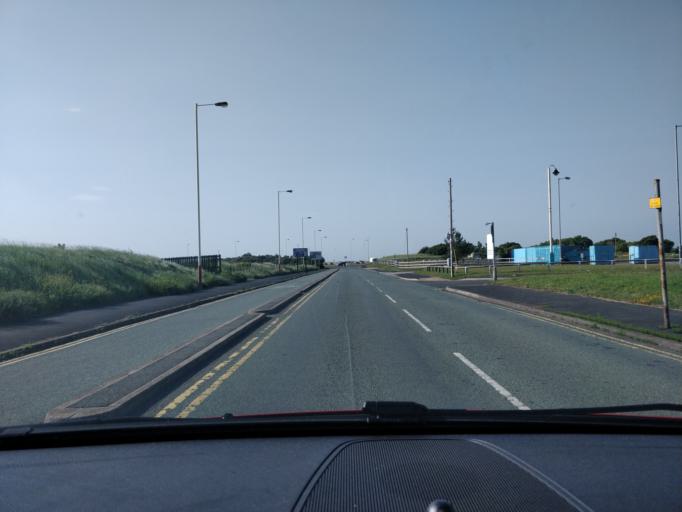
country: GB
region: England
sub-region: Sefton
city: Southport
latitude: 53.6605
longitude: -2.9979
